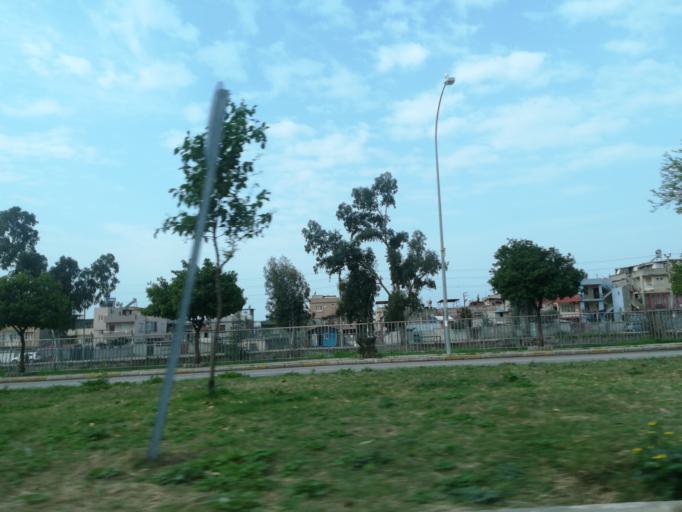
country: TR
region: Adana
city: Yuregir
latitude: 36.9942
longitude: 35.3604
